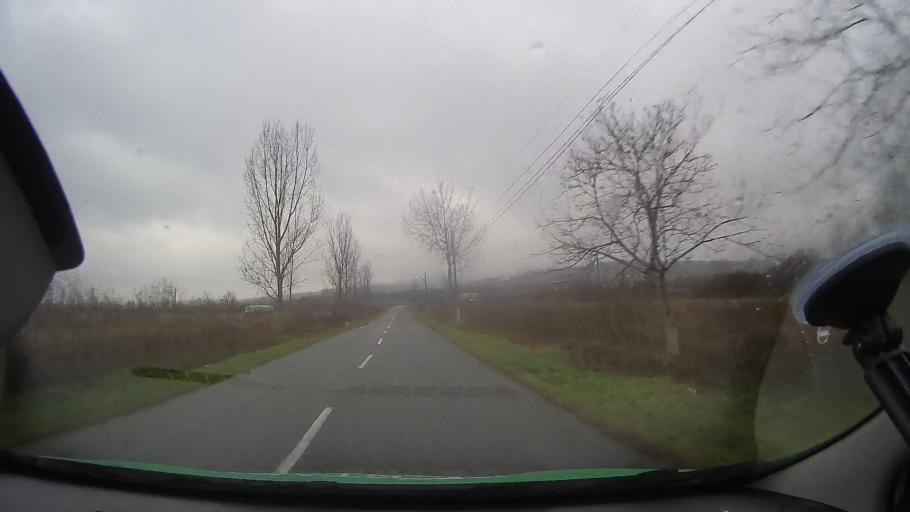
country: RO
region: Hunedoara
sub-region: Comuna Ribita
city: Ribita
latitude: 46.1658
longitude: 22.7638
